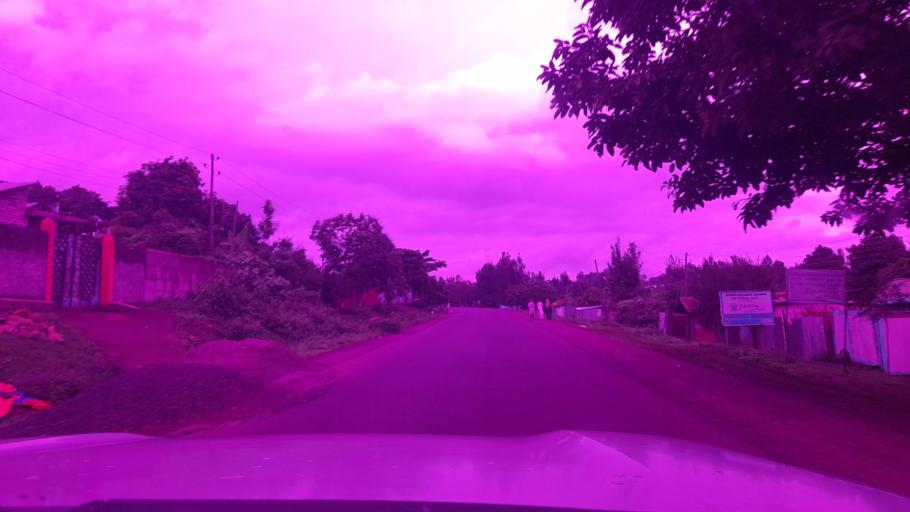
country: ET
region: Oromiya
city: Jima
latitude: 7.9277
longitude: 37.4229
